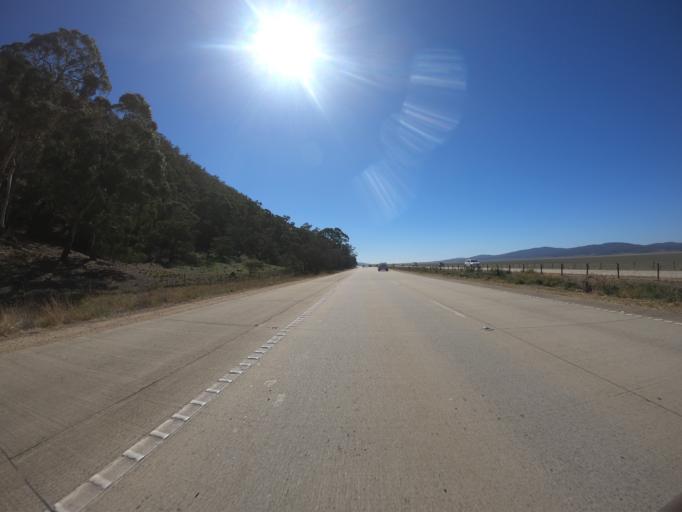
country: AU
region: New South Wales
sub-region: Yass Valley
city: Gundaroo
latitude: -35.0471
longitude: 149.3761
